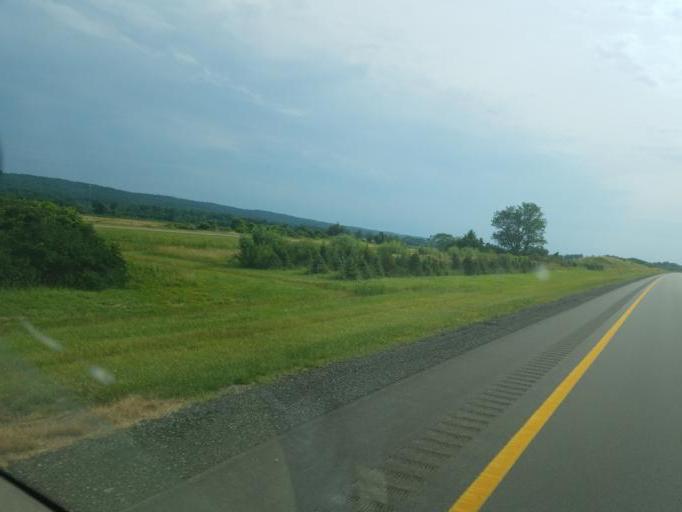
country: US
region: New York
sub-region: Chautauqua County
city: Westfield
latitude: 42.3027
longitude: -79.6490
